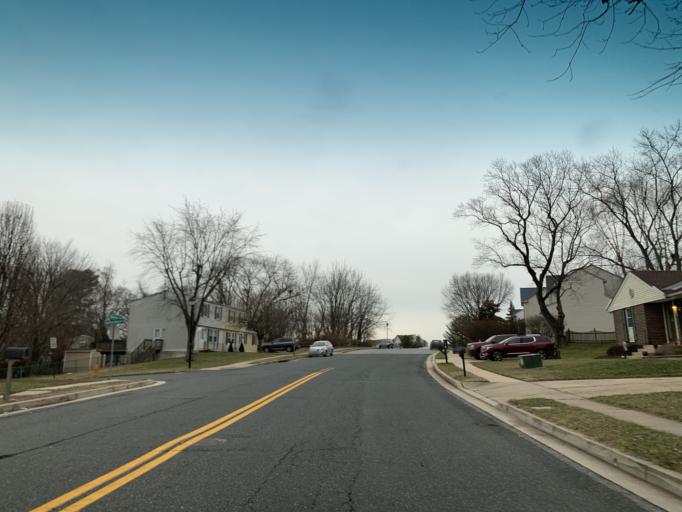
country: US
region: Maryland
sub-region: Baltimore County
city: Perry Hall
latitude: 39.3863
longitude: -76.4860
